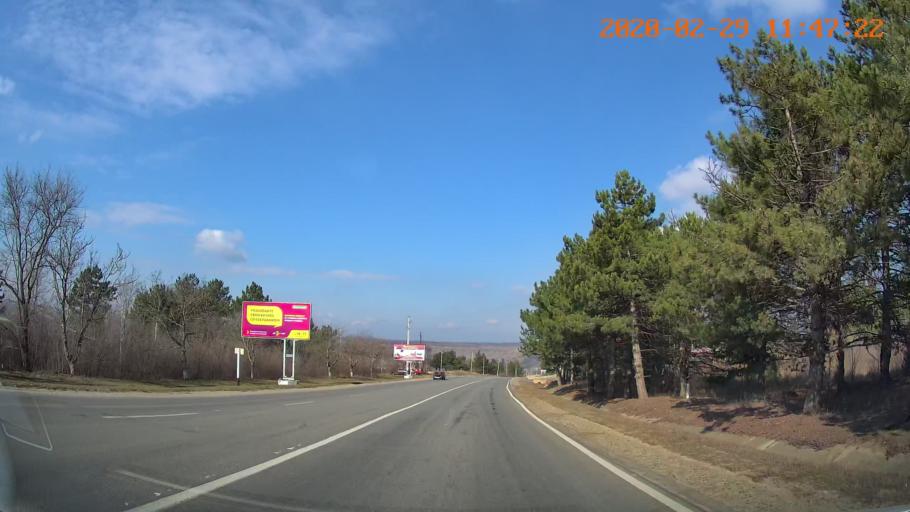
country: MD
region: Rezina
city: Rezina
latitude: 47.7399
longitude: 28.9883
